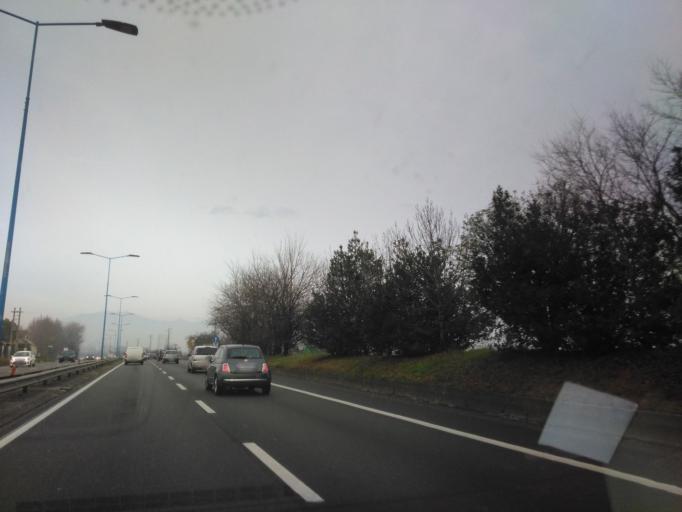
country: IT
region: Lombardy
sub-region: Provincia di Brescia
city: Roncadelle
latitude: 45.5366
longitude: 10.1809
